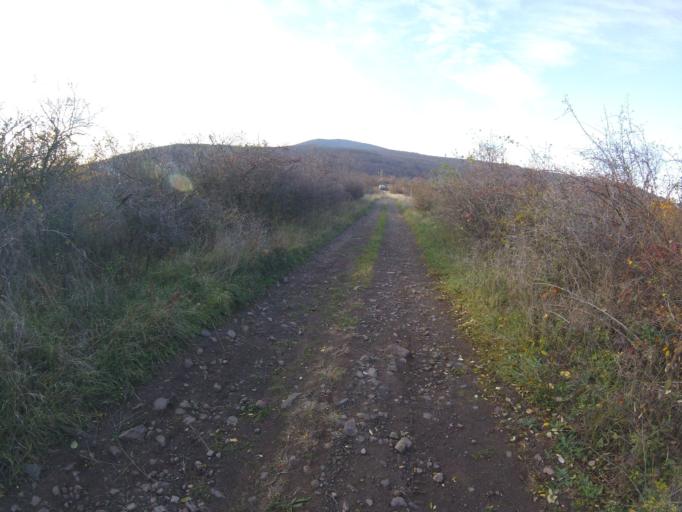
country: HU
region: Heves
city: Abasar
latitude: 47.8202
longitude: 19.9973
